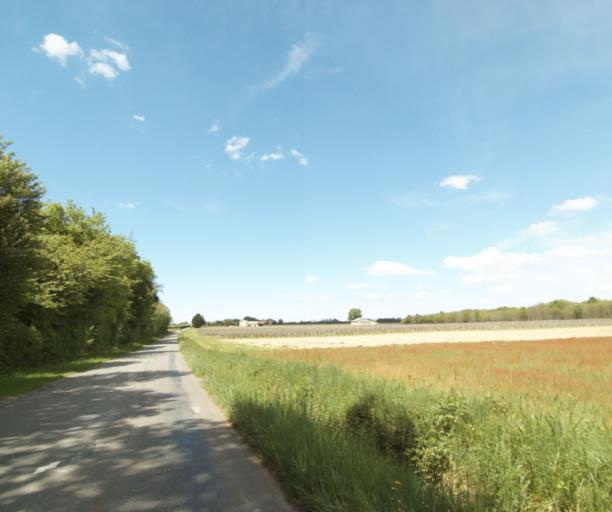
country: FR
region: Poitou-Charentes
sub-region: Departement de la Charente-Maritime
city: Burie
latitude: 45.7512
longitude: -0.4583
